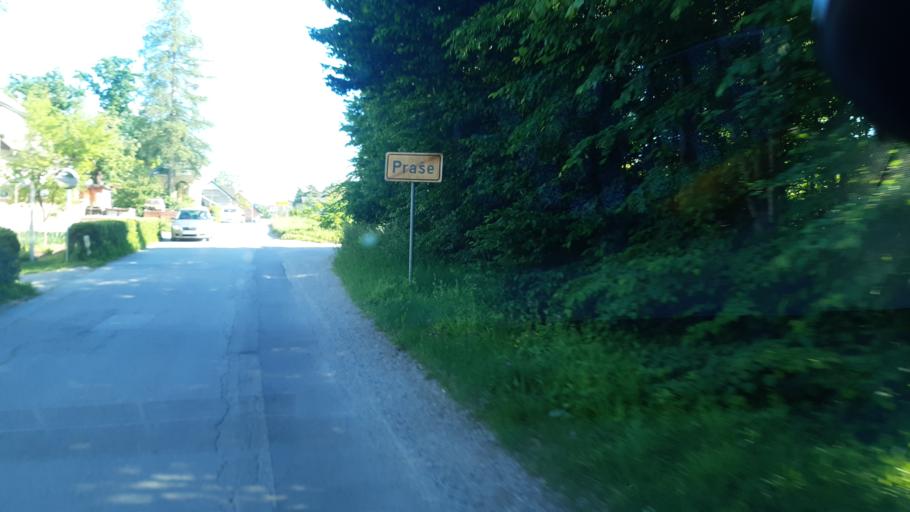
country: SI
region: Sencur
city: Hrastje
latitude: 46.1911
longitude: 14.4030
